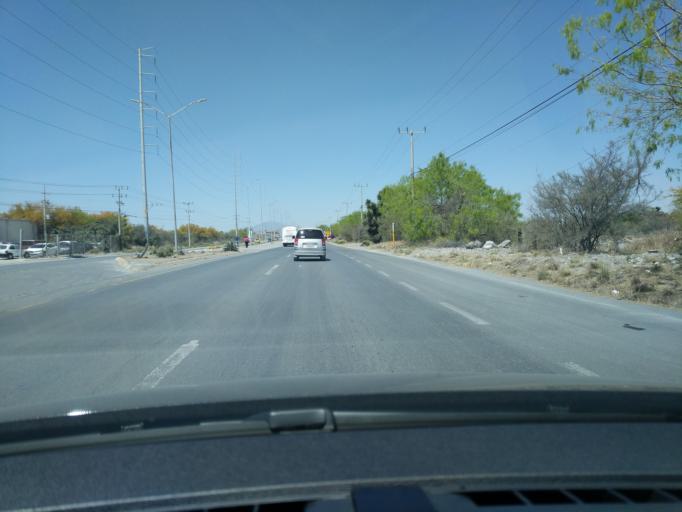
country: MX
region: Nuevo Leon
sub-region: Salinas Victoria
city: Emiliano Zapata
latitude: 25.9053
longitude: -100.2646
